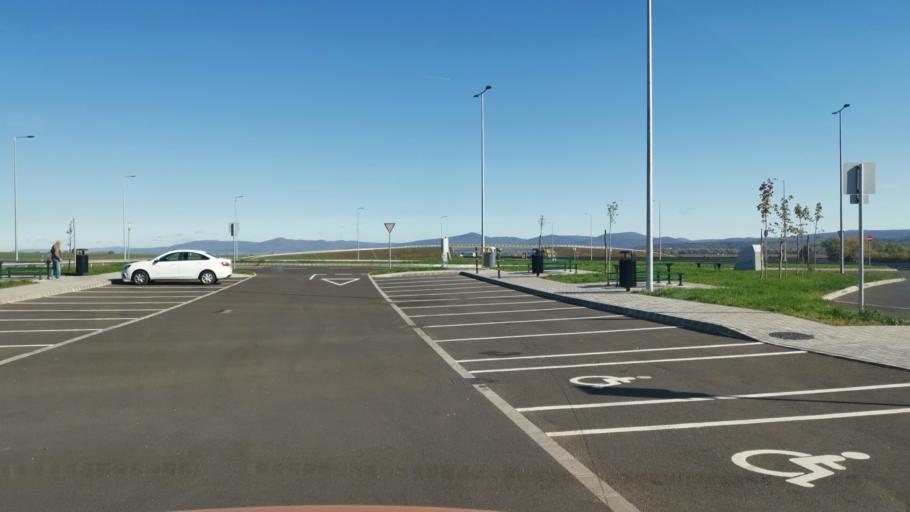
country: HU
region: Borsod-Abauj-Zemplen
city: Halmaj
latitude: 48.2941
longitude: 21.0357
